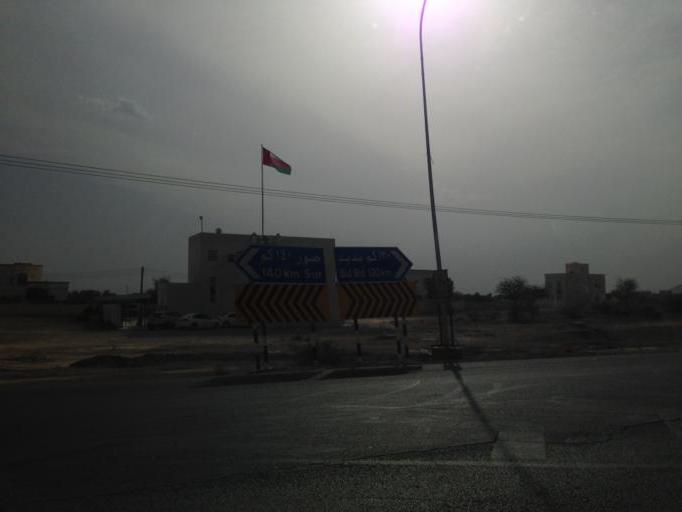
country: OM
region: Ash Sharqiyah
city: Al Qabil
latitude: 22.6075
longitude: 58.6662
